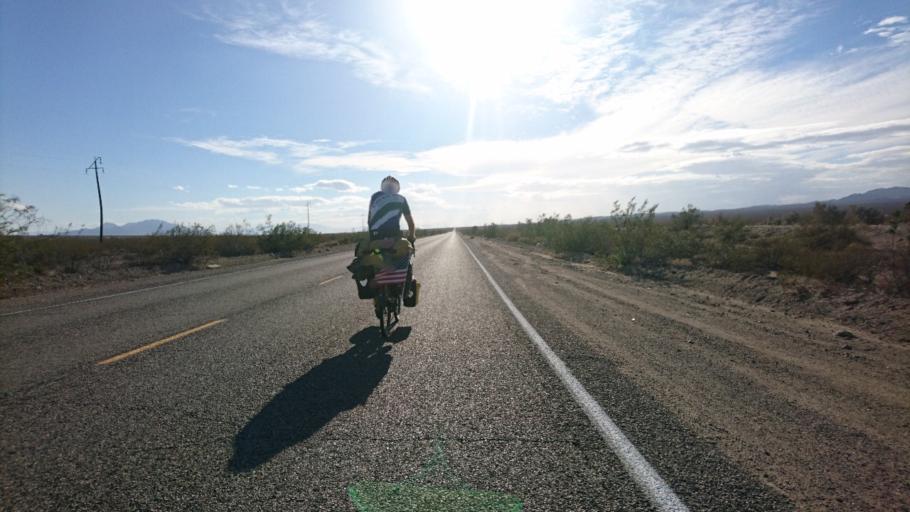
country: US
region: California
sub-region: San Bernardino County
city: Needles
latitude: 34.6986
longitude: -115.3006
